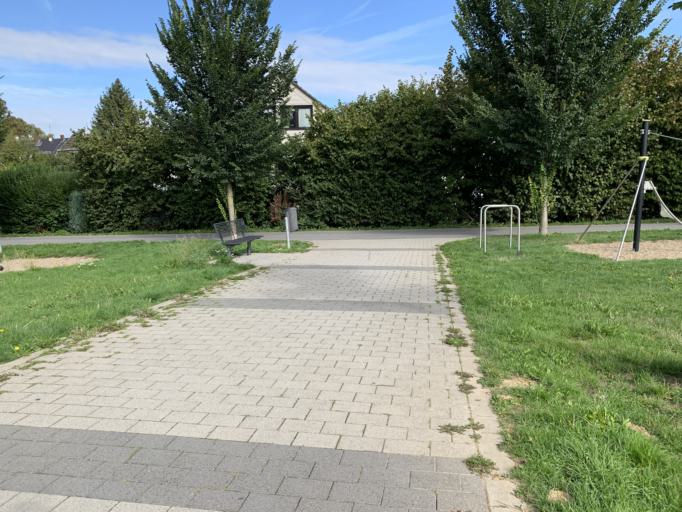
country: DE
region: North Rhine-Westphalia
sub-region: Regierungsbezirk Dusseldorf
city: Heiligenhaus
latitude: 51.3281
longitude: 6.9684
